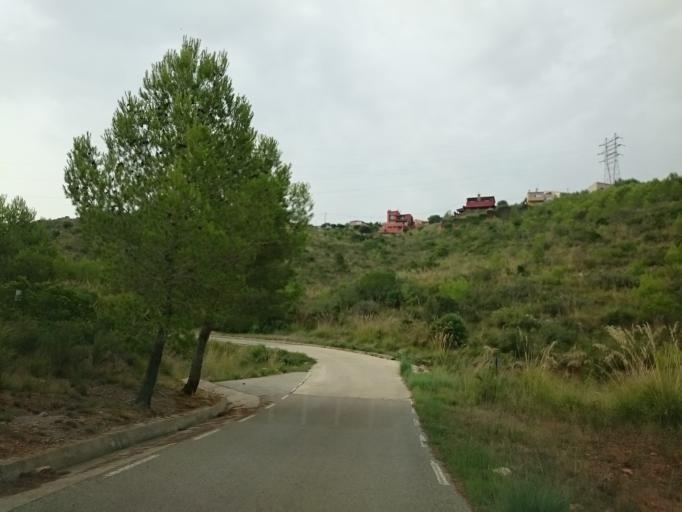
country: ES
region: Catalonia
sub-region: Provincia de Barcelona
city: Olivella
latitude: 41.2967
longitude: 1.8557
